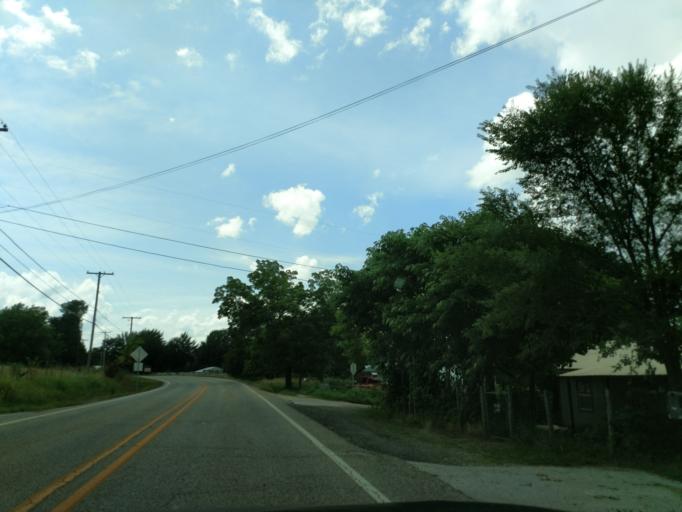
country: US
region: Arkansas
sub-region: Boone County
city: Harrison
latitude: 36.2513
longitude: -93.2171
